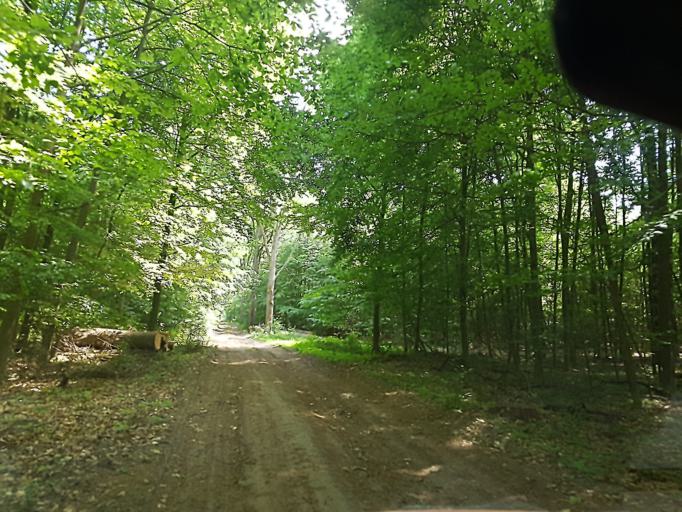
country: DE
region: Brandenburg
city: Gorzke
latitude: 52.0970
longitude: 12.3112
